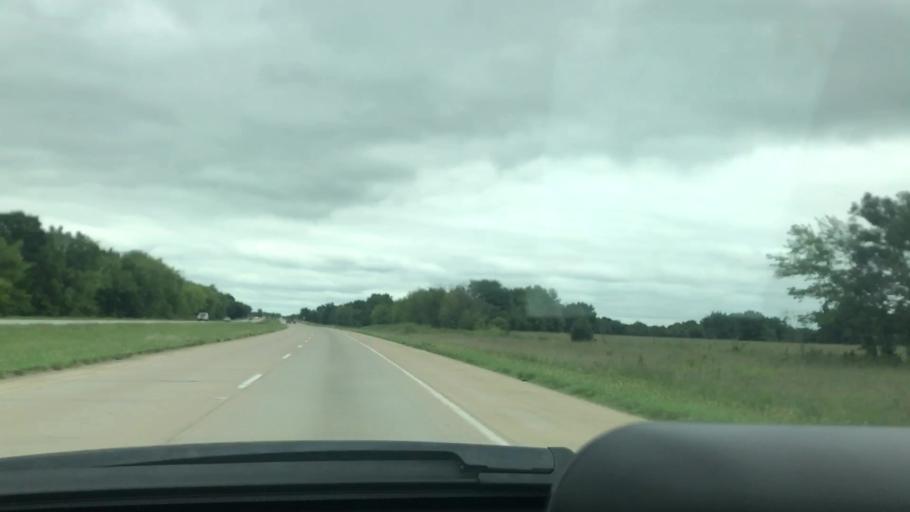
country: US
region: Oklahoma
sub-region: Mayes County
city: Chouteau
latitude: 36.2007
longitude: -95.3407
